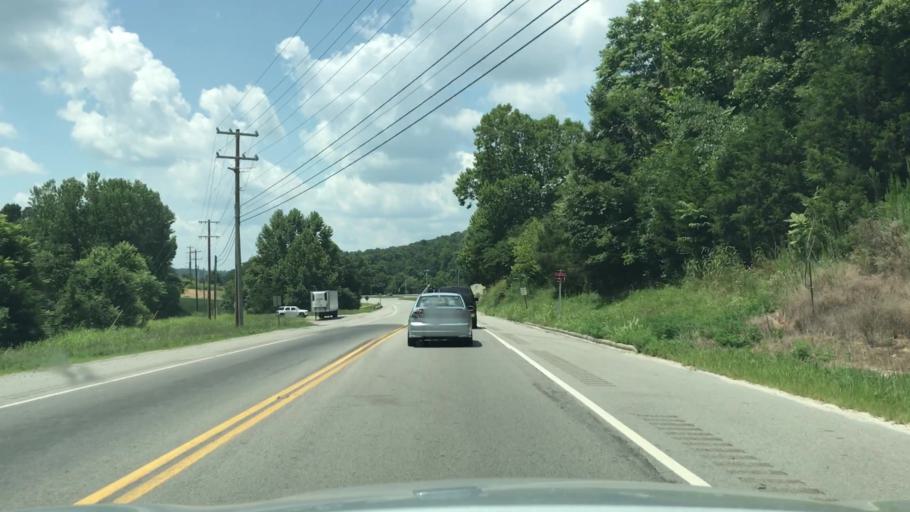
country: US
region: Tennessee
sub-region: Overton County
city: Livingston
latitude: 36.3995
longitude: -85.2979
